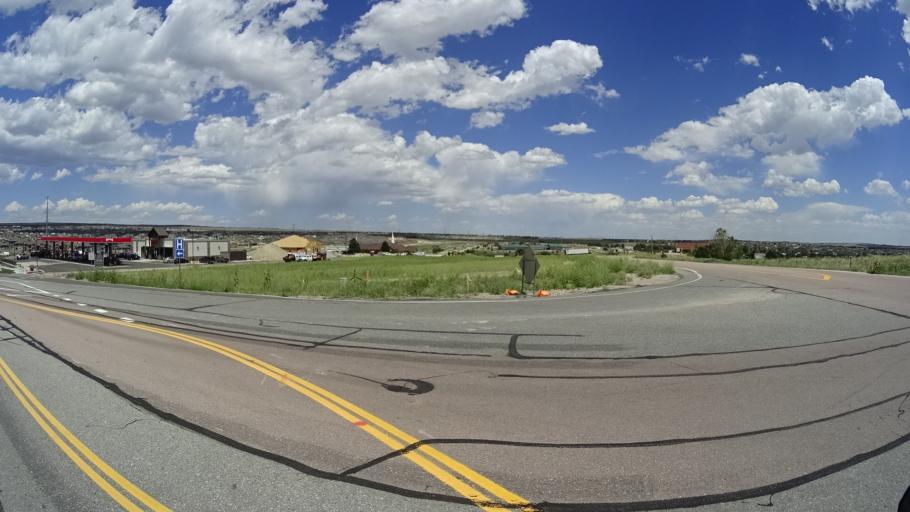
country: US
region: Colorado
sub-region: El Paso County
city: Black Forest
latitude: 38.9392
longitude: -104.7013
